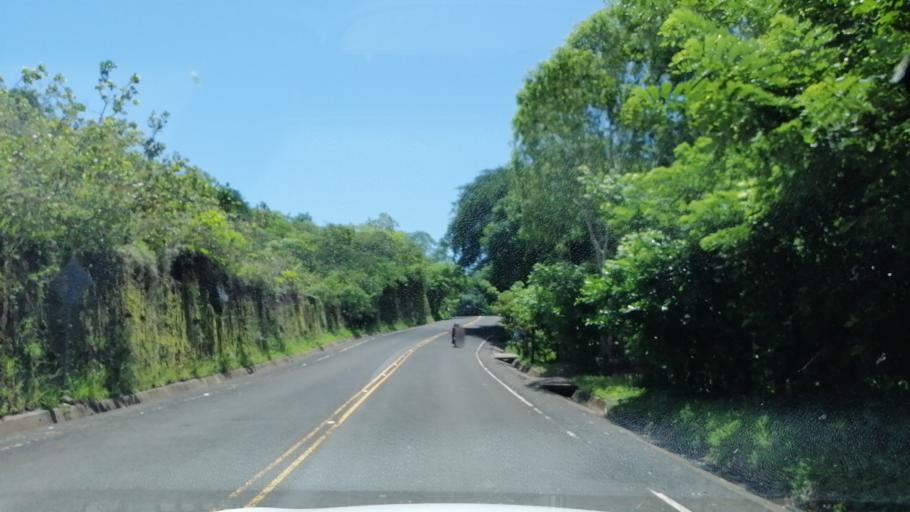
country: SV
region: San Miguel
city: Ciudad Barrios
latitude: 13.7924
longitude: -88.2871
